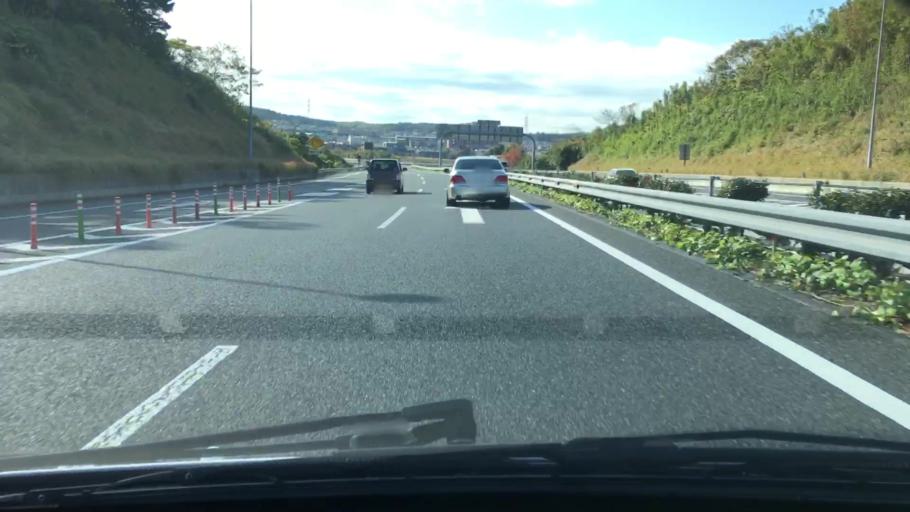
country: JP
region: Chiba
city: Kisarazu
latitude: 35.3523
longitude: 139.9469
